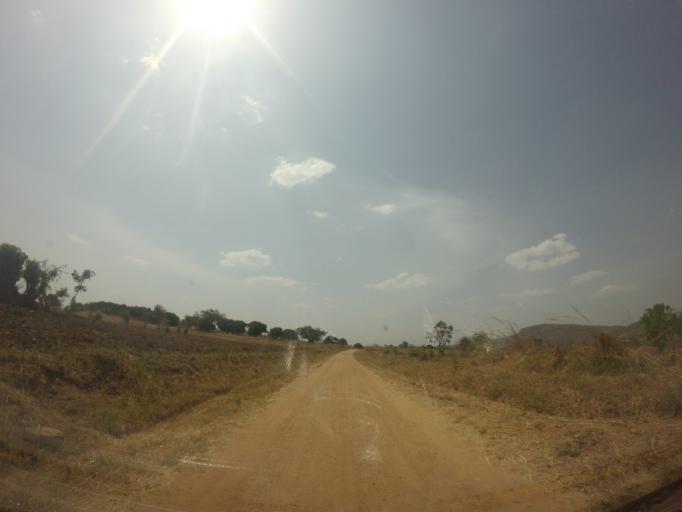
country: UG
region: Northern Region
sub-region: Arua District
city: Arua
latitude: 2.9130
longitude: 31.0417
